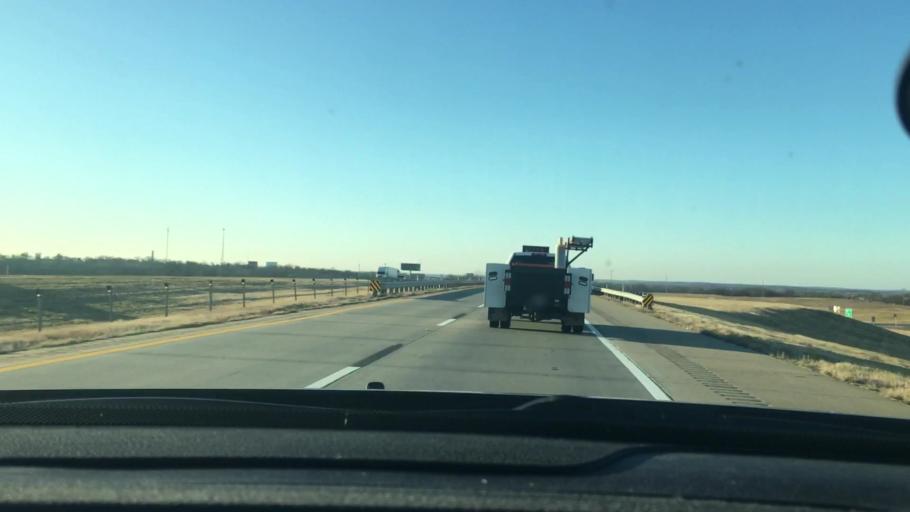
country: US
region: Oklahoma
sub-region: Carter County
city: Ardmore
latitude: 34.3346
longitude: -97.1519
